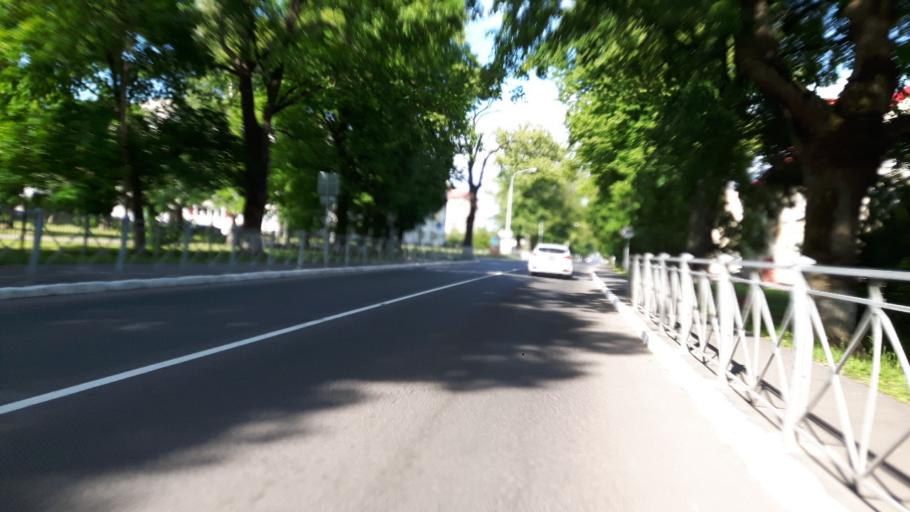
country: RU
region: Kaliningrad
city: Mamonovo
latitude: 54.4620
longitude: 19.9471
